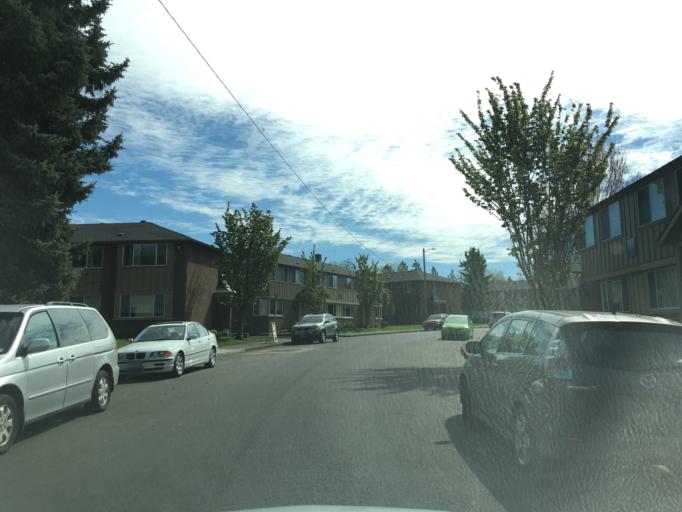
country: US
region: Oregon
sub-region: Multnomah County
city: Lents
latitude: 45.5361
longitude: -122.5963
